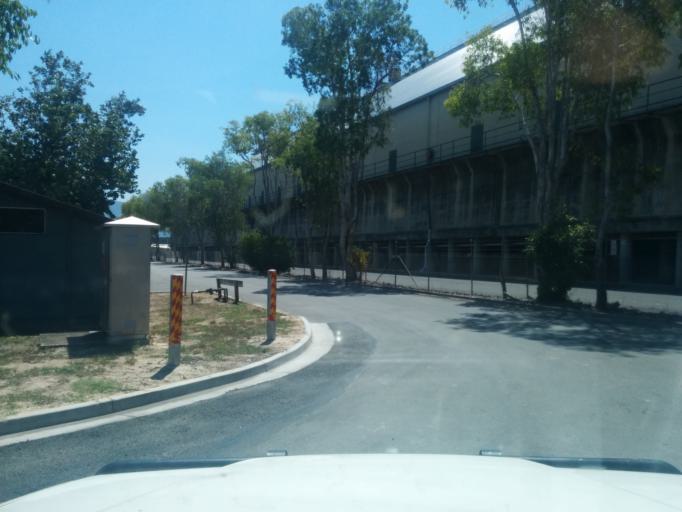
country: AU
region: Queensland
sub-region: Cairns
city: Cairns
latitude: -16.9400
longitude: 145.7772
